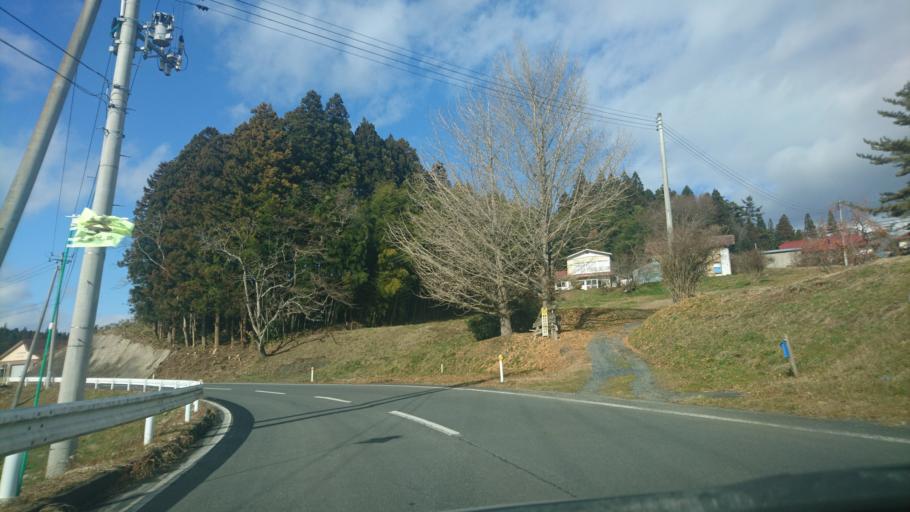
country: JP
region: Iwate
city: Ichinoseki
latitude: 38.9625
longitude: 141.4126
